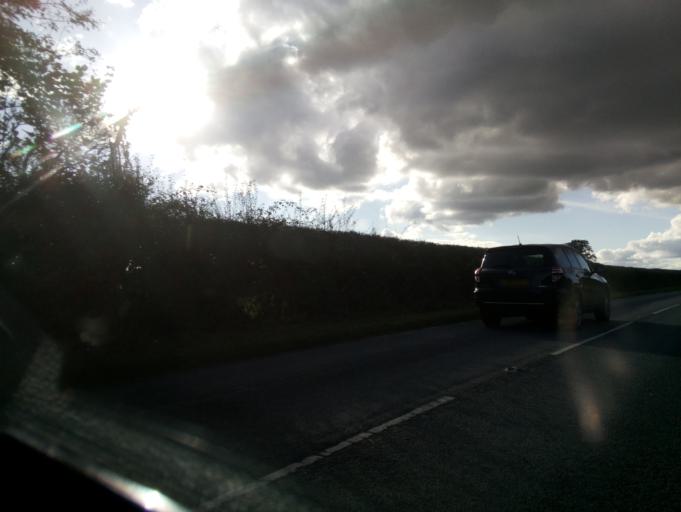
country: GB
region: Wales
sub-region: Sir Powys
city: Hay
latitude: 52.0681
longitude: -3.1416
